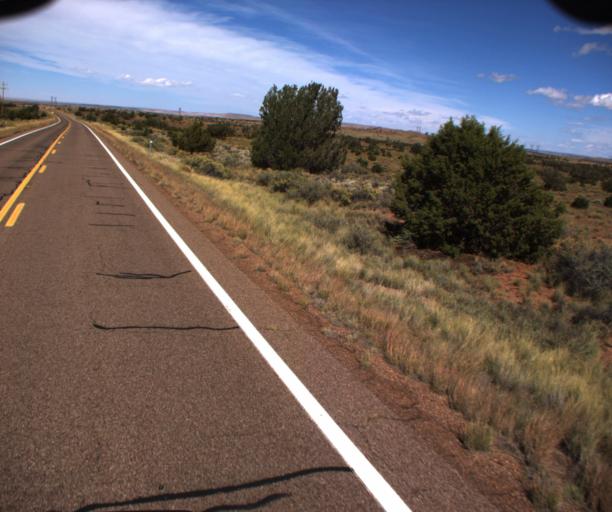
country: US
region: Arizona
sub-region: Apache County
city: Saint Johns
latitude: 34.5297
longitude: -109.6203
